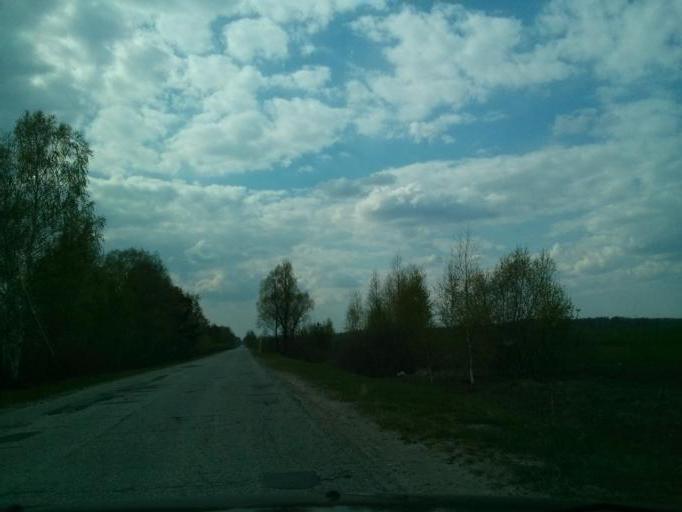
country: RU
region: Nizjnij Novgorod
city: Shimorskoye
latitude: 55.3366
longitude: 41.9033
